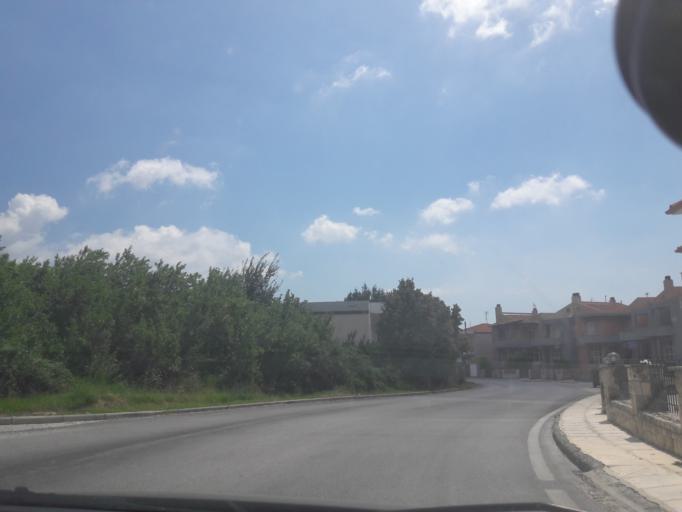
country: GR
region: Central Macedonia
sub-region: Nomos Chalkidikis
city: Polygyros
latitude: 40.3771
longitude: 23.4501
